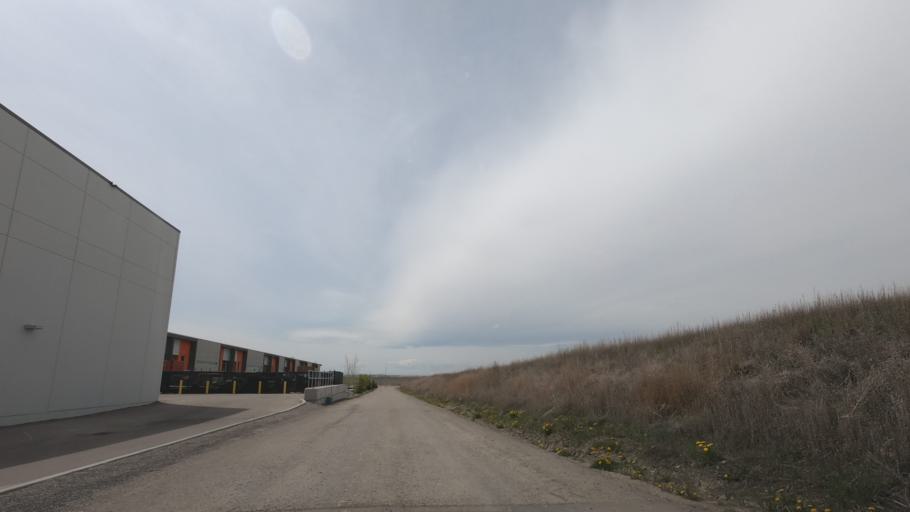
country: CA
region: Alberta
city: Airdrie
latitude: 51.3051
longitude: -113.9817
